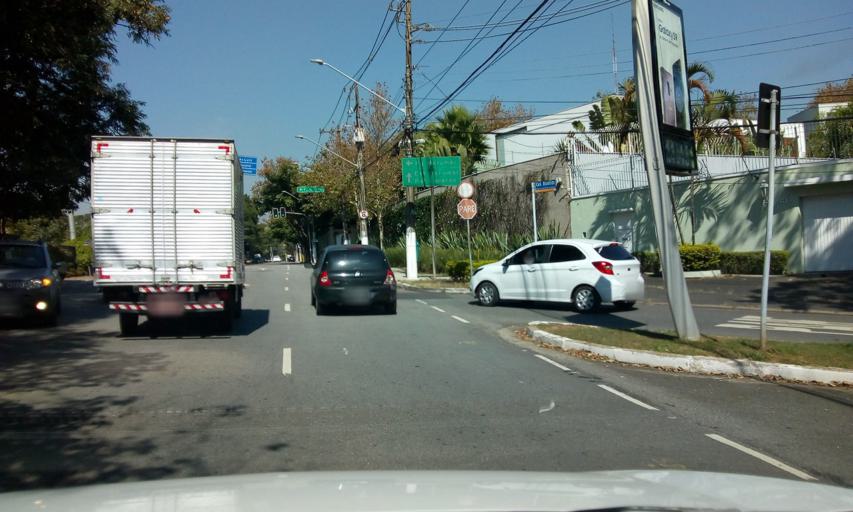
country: BR
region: Sao Paulo
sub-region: Sao Paulo
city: Sao Paulo
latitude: -23.5863
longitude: -46.7060
